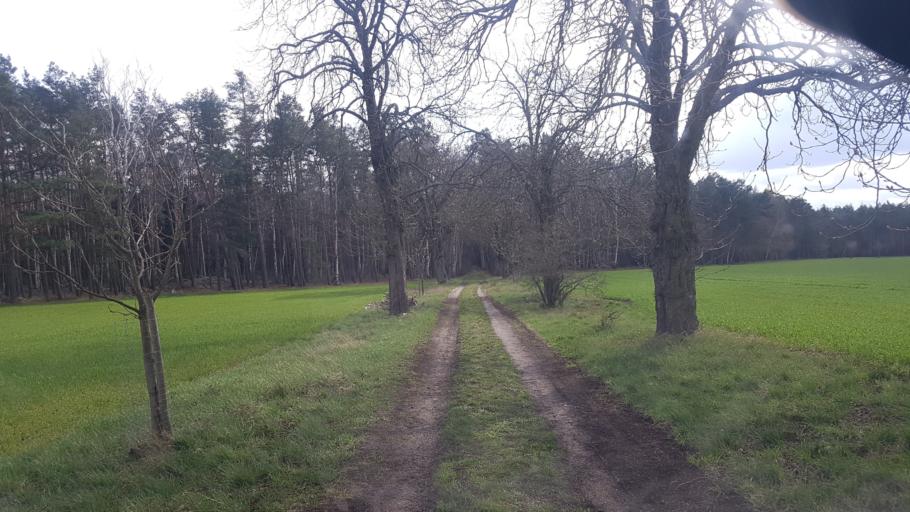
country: DE
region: Brandenburg
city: Hohenbucko
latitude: 51.6859
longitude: 13.4672
